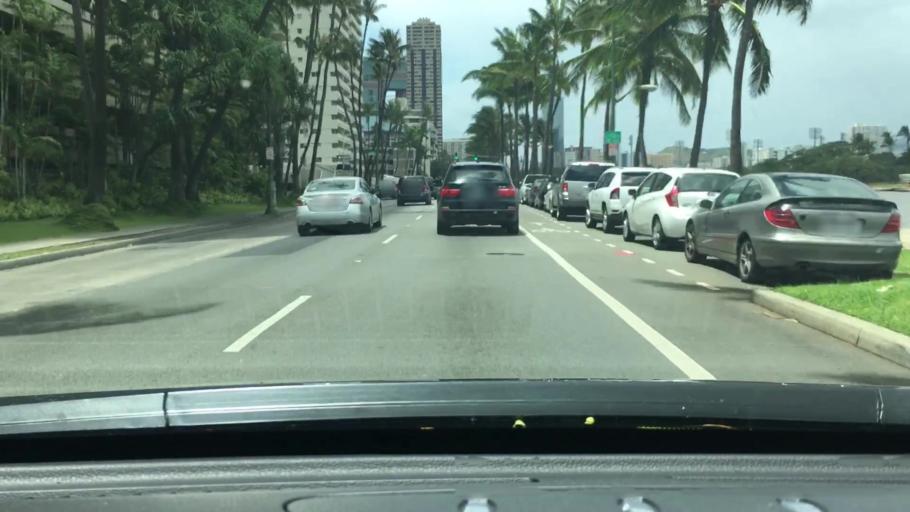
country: US
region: Hawaii
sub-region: Honolulu County
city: Honolulu
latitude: 21.2835
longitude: -157.8279
